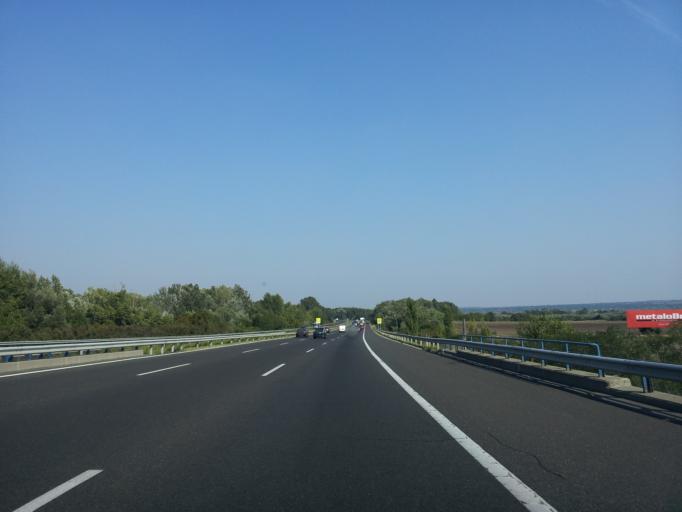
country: HU
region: Fejer
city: Gardony
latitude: 47.2317
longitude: 18.5904
